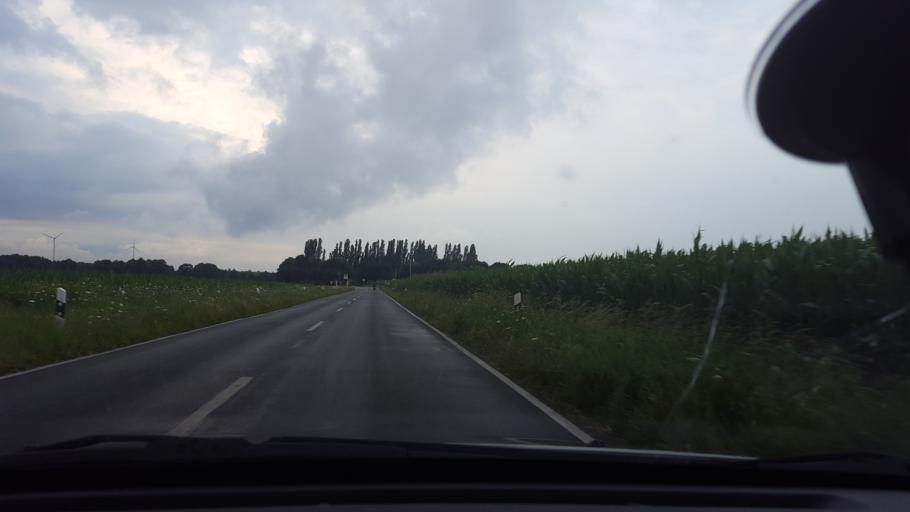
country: DE
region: North Rhine-Westphalia
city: Herten
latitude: 51.6448
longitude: 7.1563
